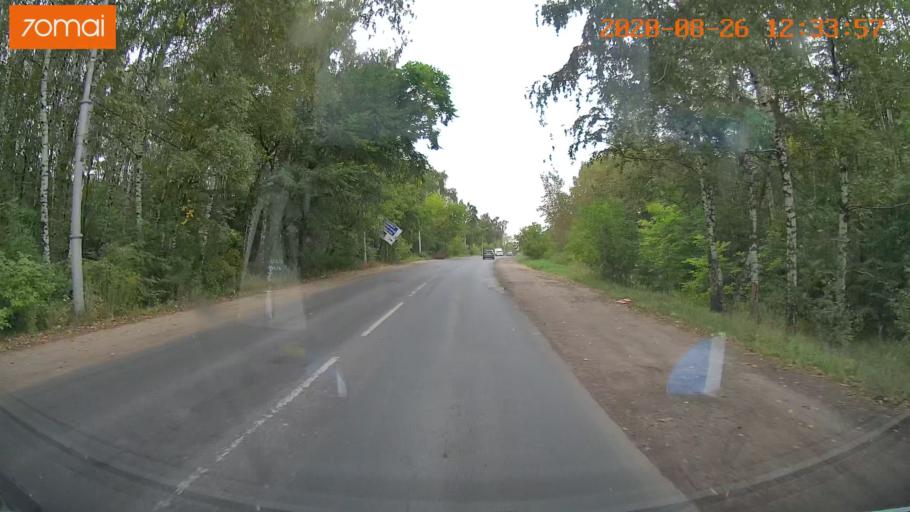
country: RU
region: Rjazan
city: Ryazan'
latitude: 54.5844
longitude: 39.7731
